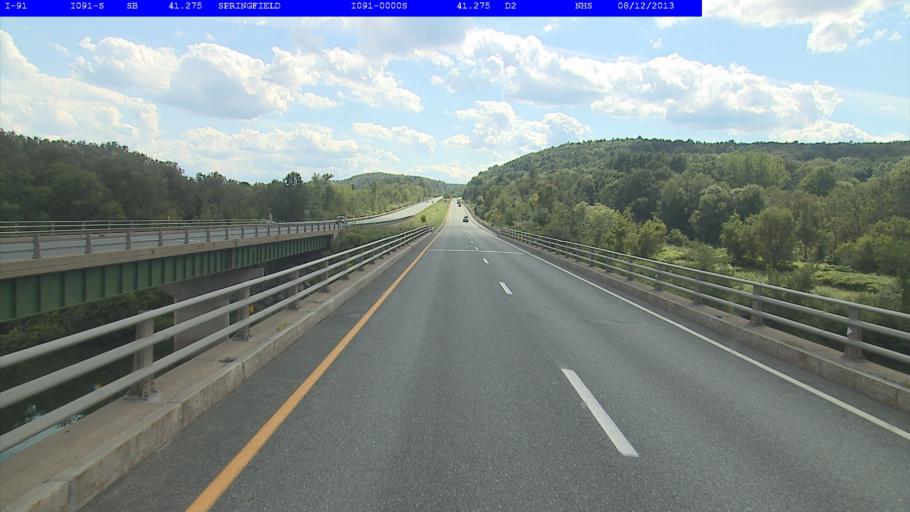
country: US
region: New Hampshire
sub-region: Sullivan County
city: Charlestown
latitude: 43.2614
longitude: -72.4358
